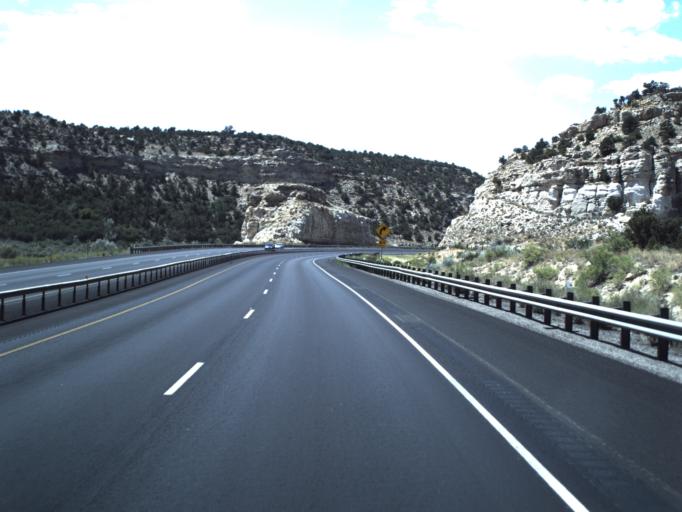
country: US
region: Utah
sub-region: Sevier County
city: Salina
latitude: 38.9098
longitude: -111.7051
